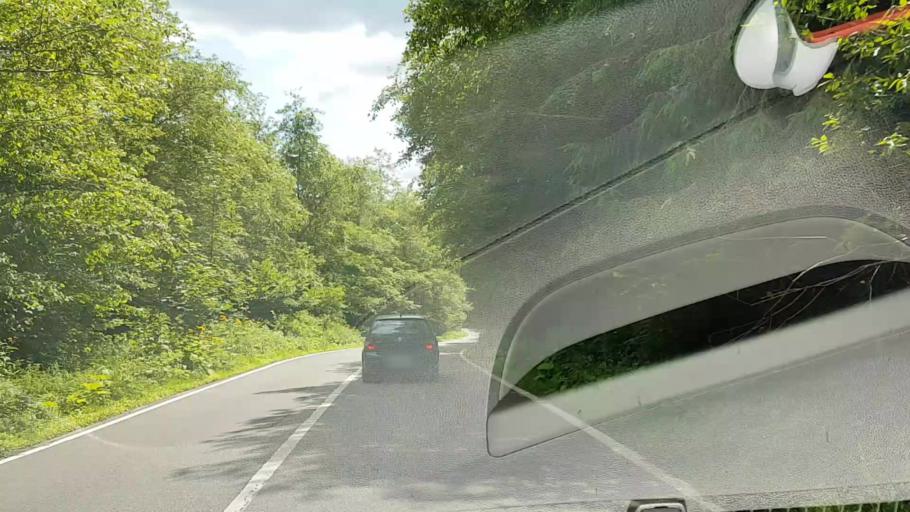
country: RO
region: Suceava
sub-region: Comuna Crucea
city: Crucea
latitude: 47.2909
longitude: 25.6326
